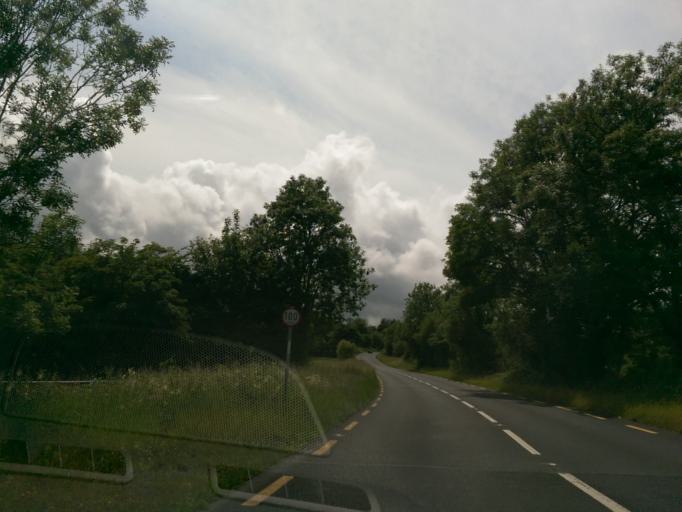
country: IE
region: Munster
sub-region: An Clar
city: Ennis
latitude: 52.8204
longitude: -9.0141
